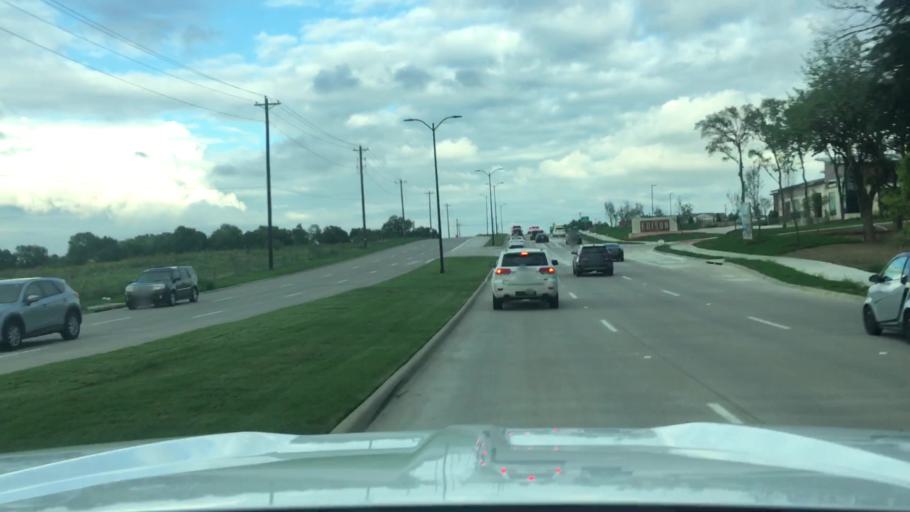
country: US
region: Texas
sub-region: Collin County
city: Frisco
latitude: 33.1746
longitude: -96.8072
